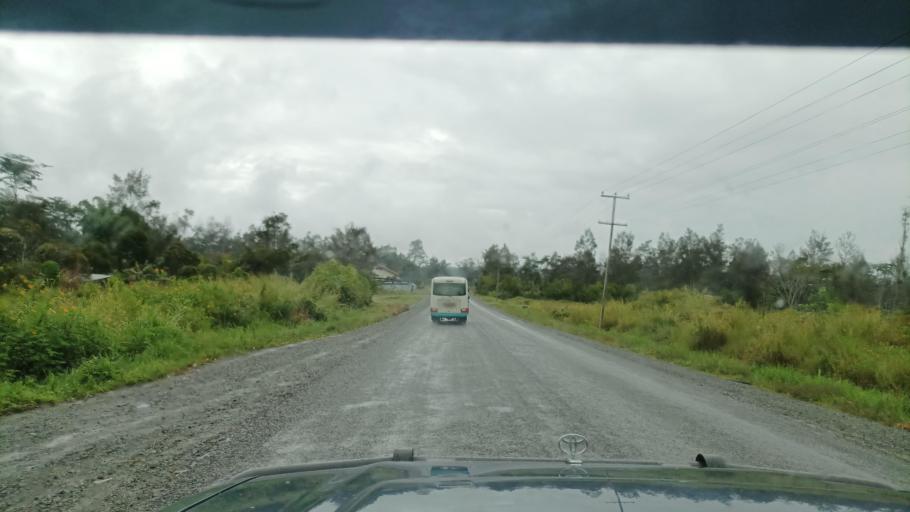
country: PG
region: Western Highlands
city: Rauna
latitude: -5.8247
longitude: 144.3817
